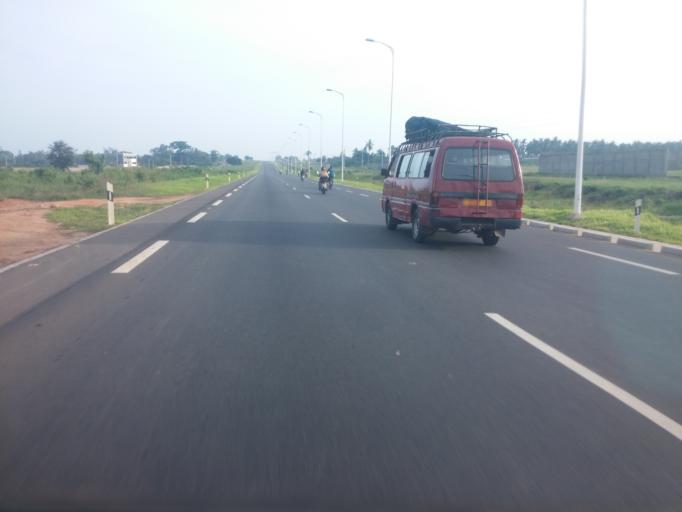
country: TG
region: Maritime
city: Tsevie
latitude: 6.3327
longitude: 1.2174
